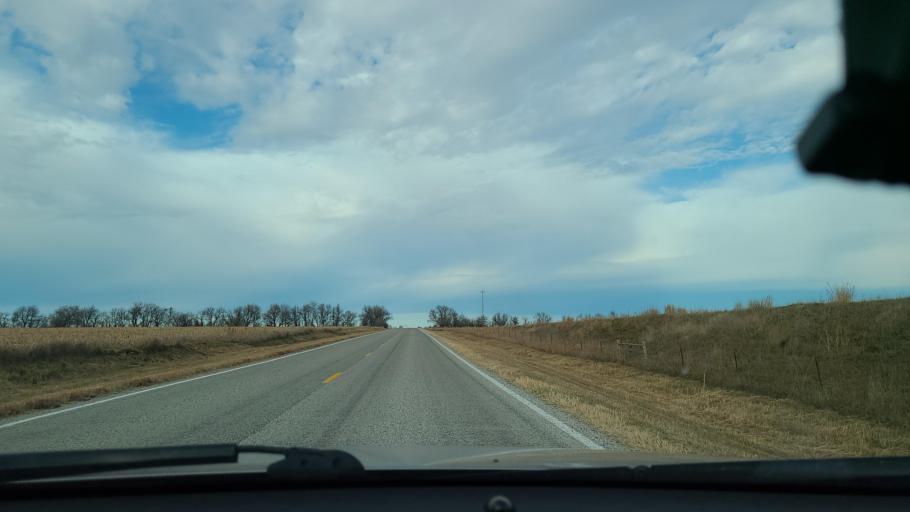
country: US
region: Kansas
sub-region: McPherson County
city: Inman
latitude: 38.3522
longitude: -97.9244
